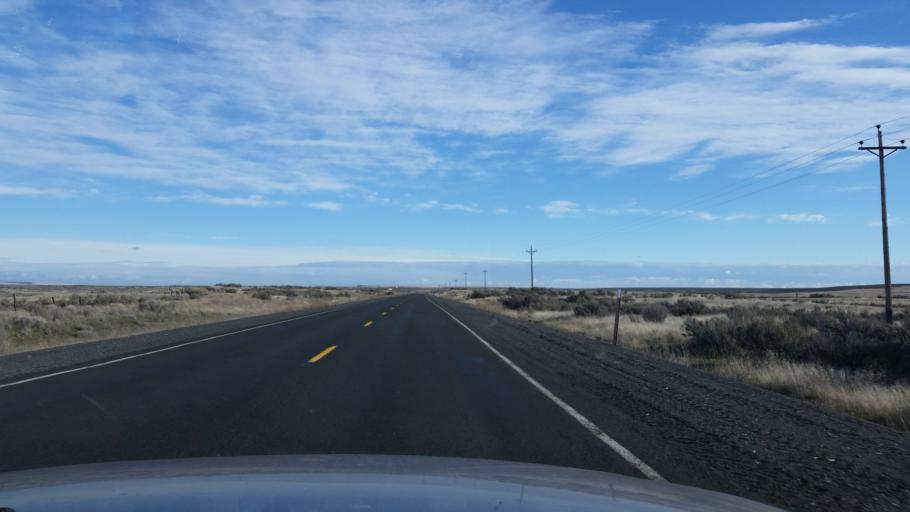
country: US
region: Washington
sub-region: Grant County
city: Warden
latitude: 47.3134
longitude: -118.7761
